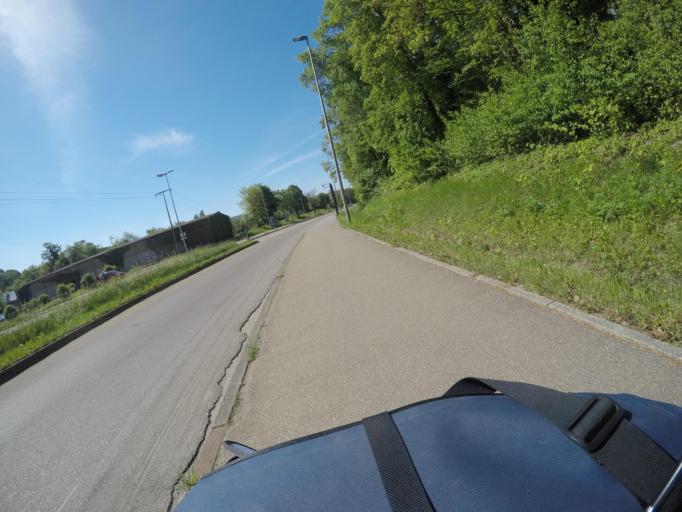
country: DE
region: Baden-Wuerttemberg
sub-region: Regierungsbezirk Stuttgart
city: Aalen
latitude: 48.8568
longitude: 10.0981
